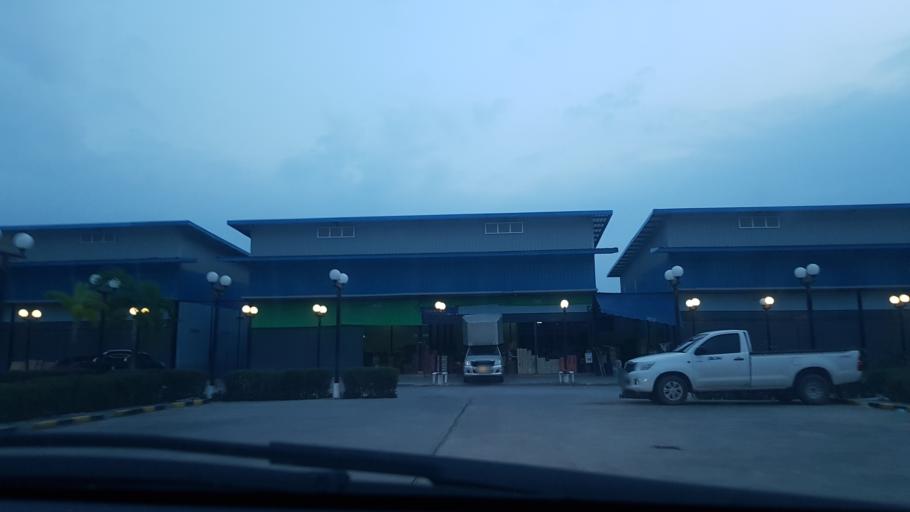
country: TH
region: Bangkok
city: Nong Khaem
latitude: 13.7461
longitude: 100.3658
